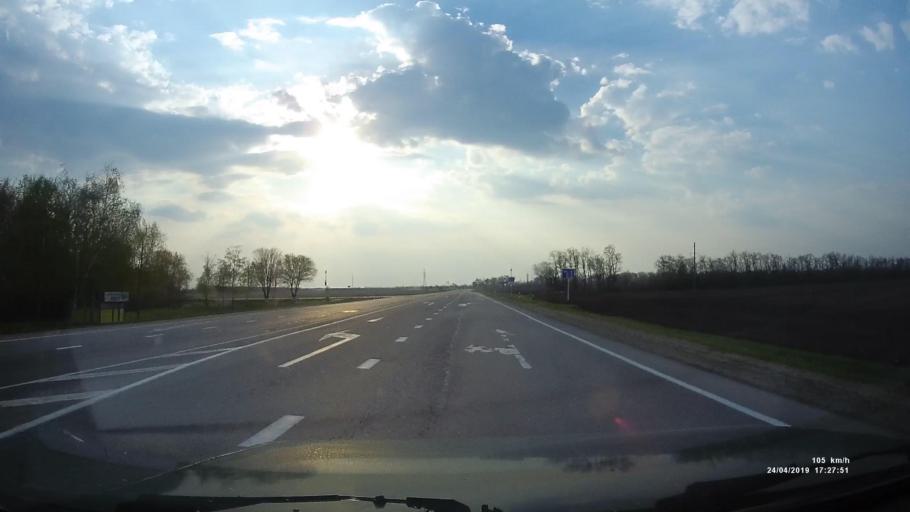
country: RU
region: Rostov
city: Gigant
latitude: 46.5300
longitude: 41.1898
